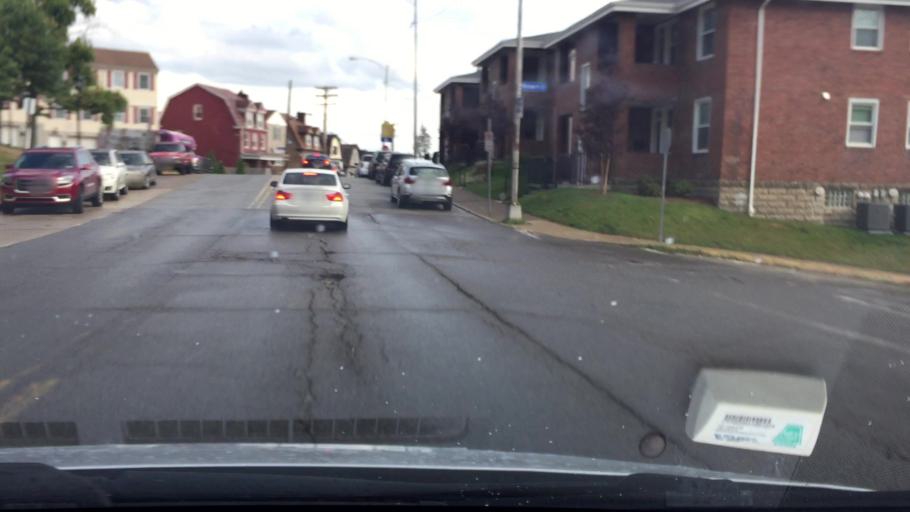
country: US
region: Pennsylvania
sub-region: Allegheny County
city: Bloomfield
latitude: 40.4435
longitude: -79.9662
